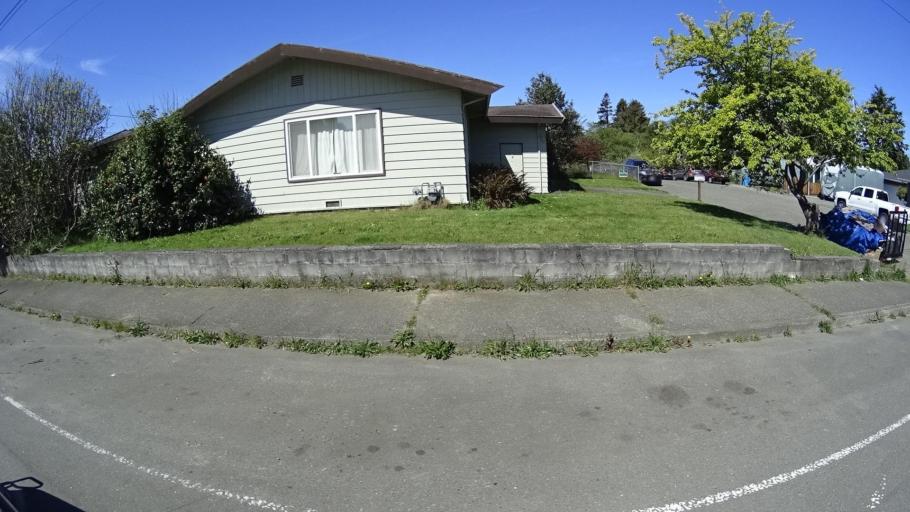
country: US
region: California
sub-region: Humboldt County
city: Myrtletown
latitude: 40.7935
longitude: -124.1263
